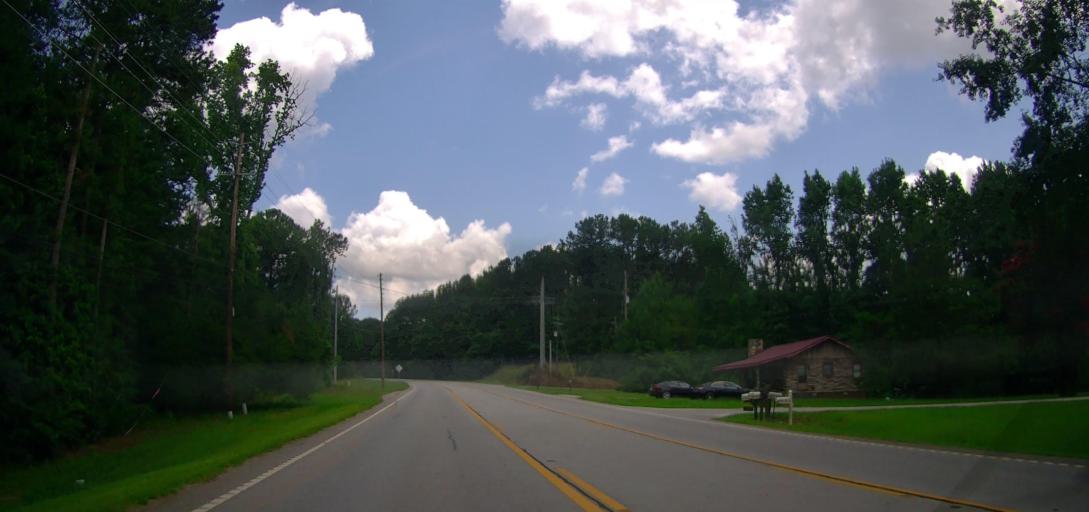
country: US
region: Georgia
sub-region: Heard County
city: Franklin
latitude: 33.2677
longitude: -85.0832
